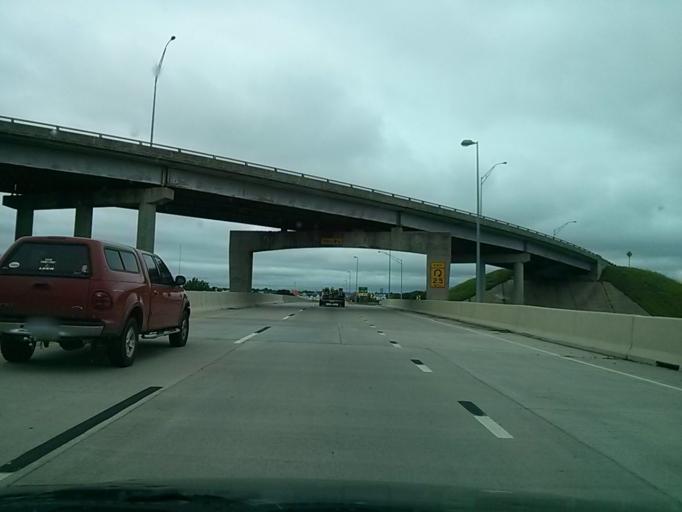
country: US
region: Oklahoma
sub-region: Tulsa County
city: Owasso
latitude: 36.1658
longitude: -95.8603
